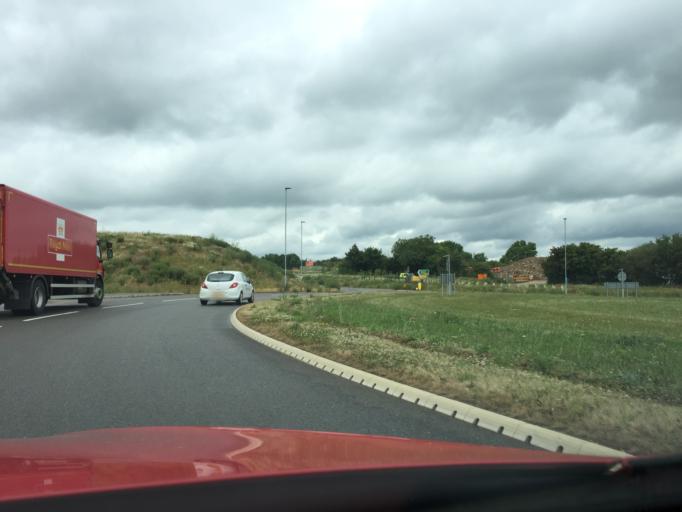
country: GB
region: England
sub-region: Northamptonshire
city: Bugbrooke
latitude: 52.2296
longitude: -1.0212
